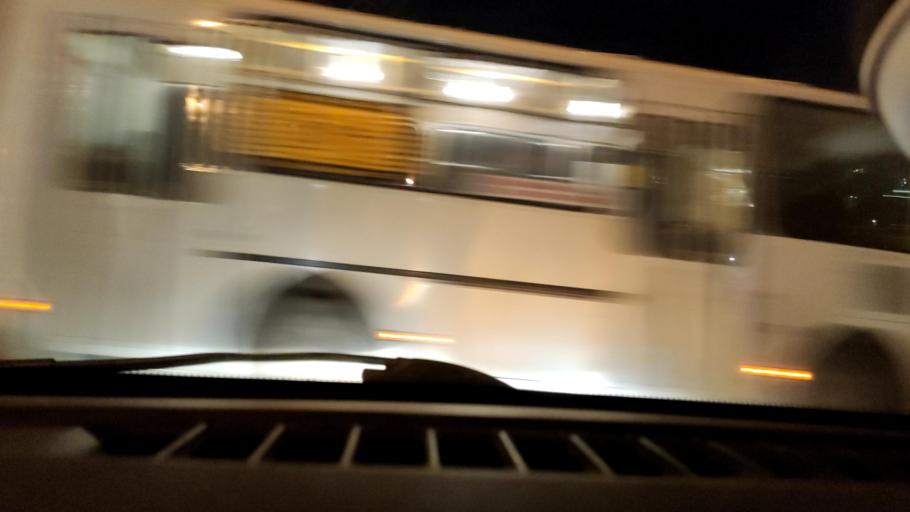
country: RU
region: Samara
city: Samara
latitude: 53.1971
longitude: 50.1999
